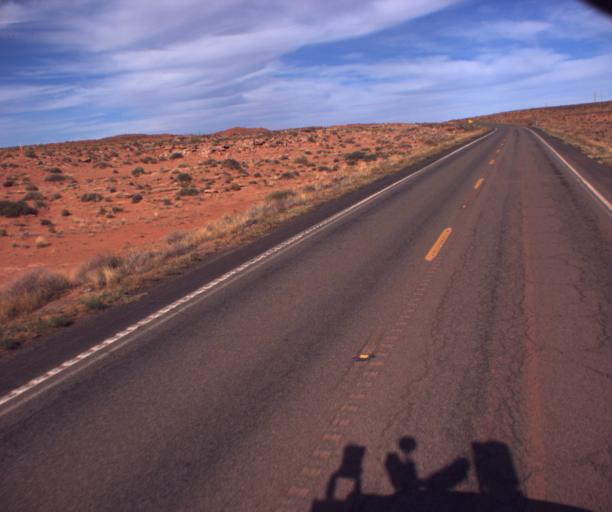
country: US
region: Arizona
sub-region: Navajo County
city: Kayenta
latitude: 36.8945
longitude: -109.7976
